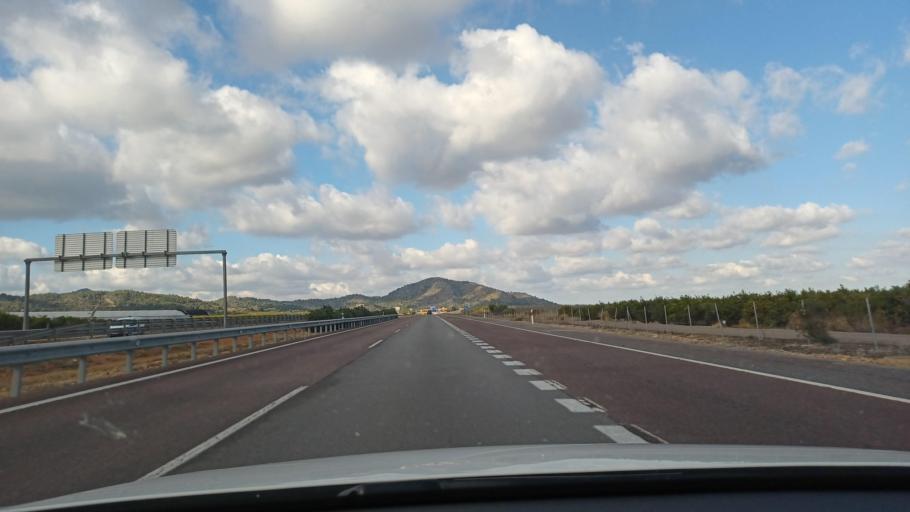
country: ES
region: Valencia
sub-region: Provincia de Castello
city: Villavieja
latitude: 39.8792
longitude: -0.1921
